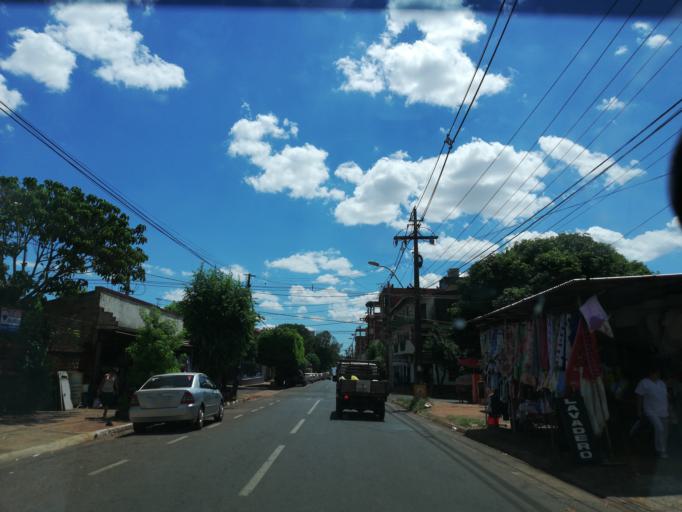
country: PY
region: Itapua
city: Encarnacion
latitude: -27.3406
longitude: -55.8619
